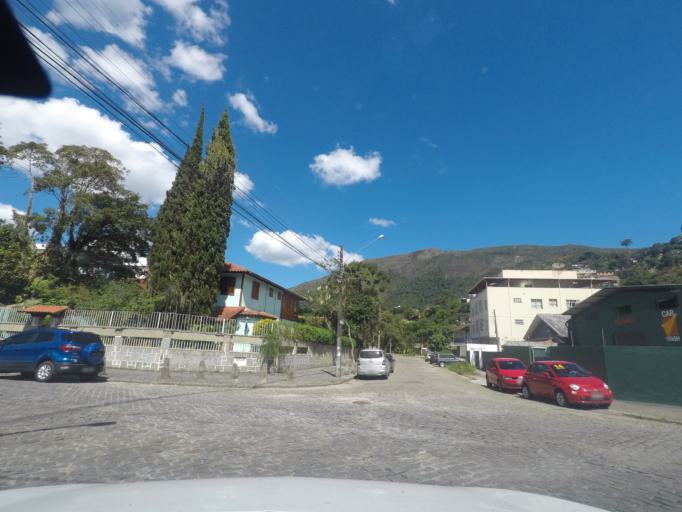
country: BR
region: Rio de Janeiro
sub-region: Teresopolis
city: Teresopolis
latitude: -22.4359
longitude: -42.9765
